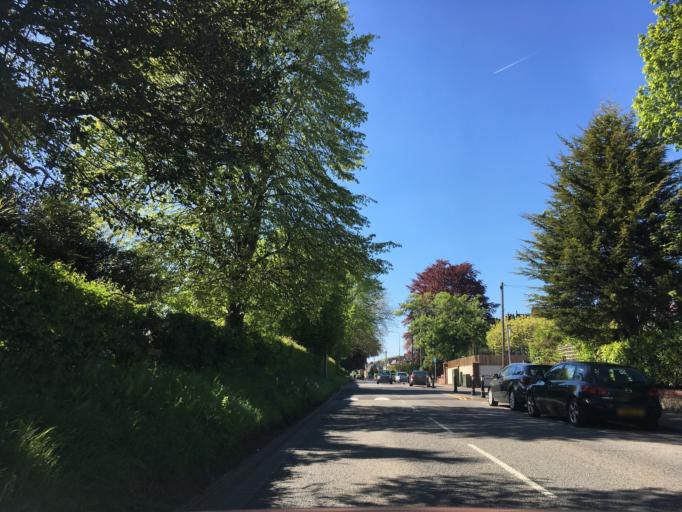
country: GB
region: Wales
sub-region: Cardiff
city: Radyr
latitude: 51.5163
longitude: -3.2252
